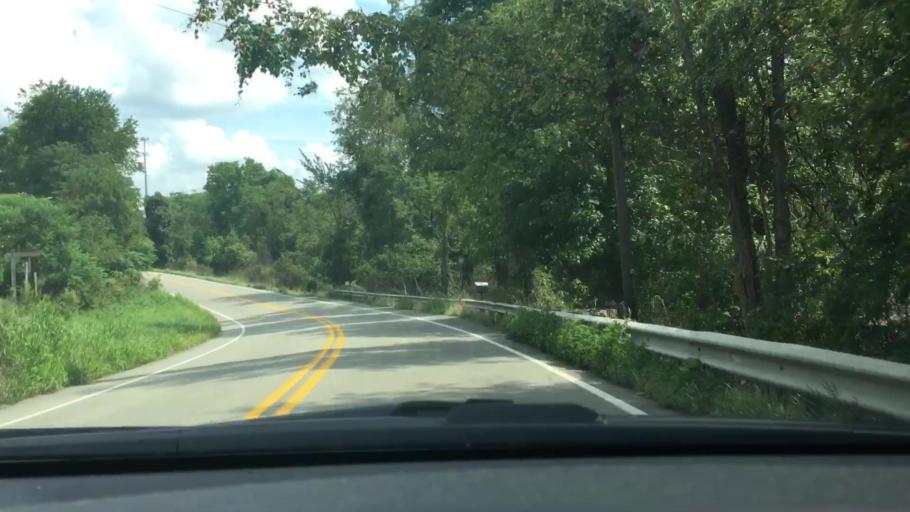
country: US
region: Pennsylvania
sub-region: Washington County
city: McMurray
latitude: 40.2363
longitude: -80.0832
